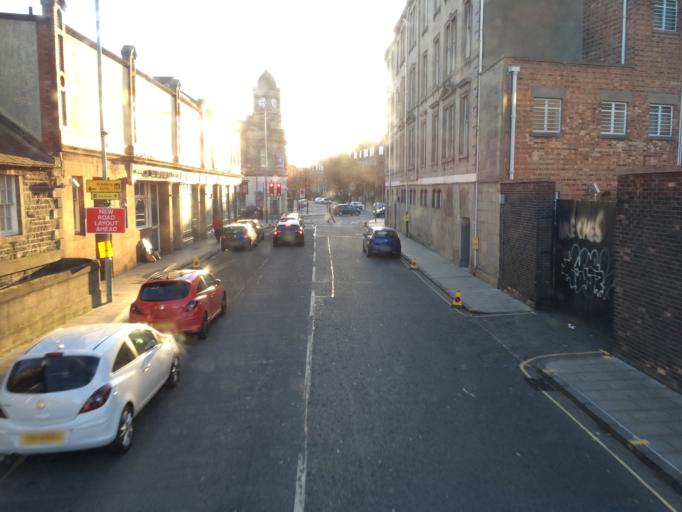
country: GB
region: Scotland
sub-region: West Lothian
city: Seafield
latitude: 55.9711
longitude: -3.1706
